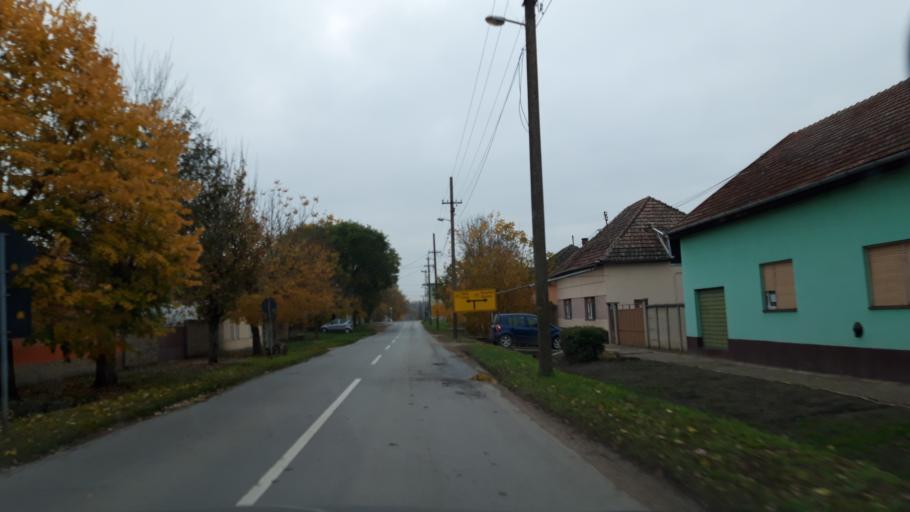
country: RS
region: Autonomna Pokrajina Vojvodina
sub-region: Severnobanatski Okrug
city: Novi Knezevac
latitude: 46.0404
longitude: 20.0922
